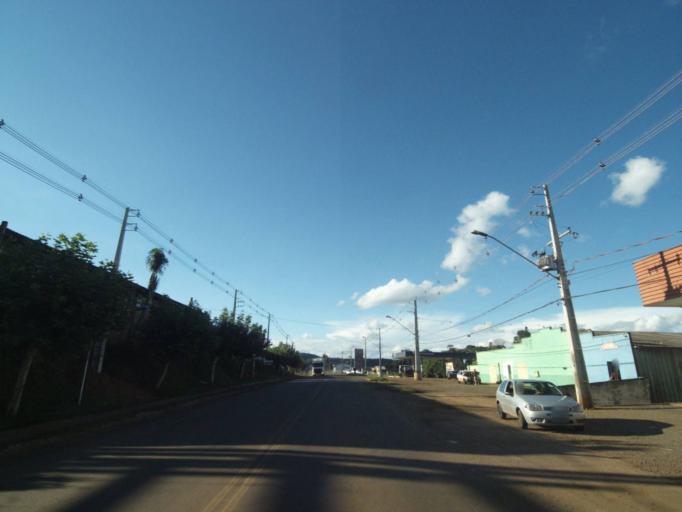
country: BR
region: Parana
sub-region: Uniao Da Vitoria
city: Uniao da Vitoria
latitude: -26.1641
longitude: -51.5364
